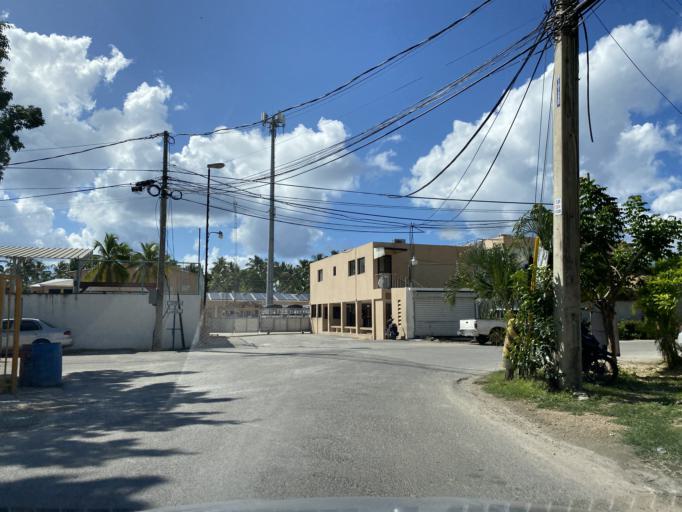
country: DO
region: La Romana
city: La Romana
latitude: 18.3505
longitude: -68.8302
